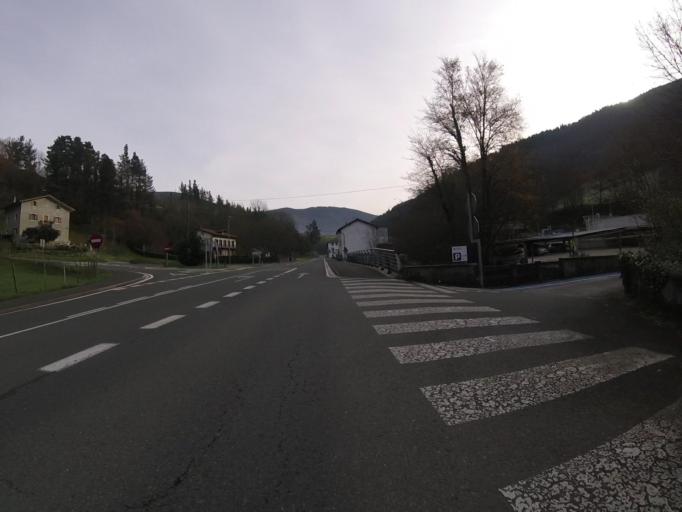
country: ES
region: Basque Country
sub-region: Provincia de Guipuzcoa
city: Berrobi
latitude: 43.1433
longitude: -2.0165
